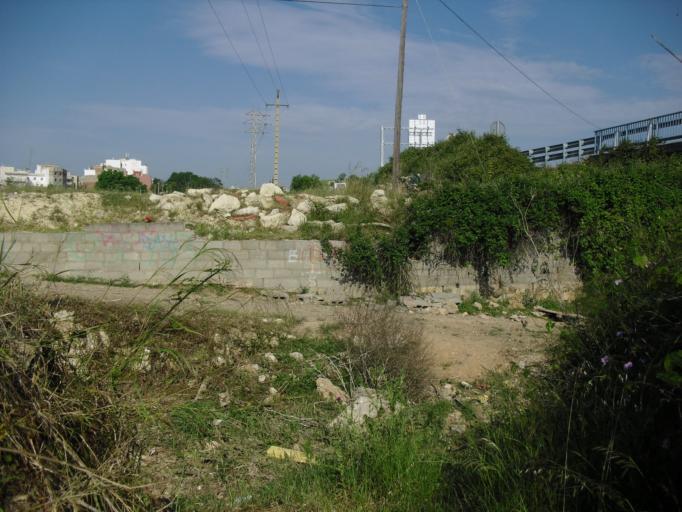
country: ES
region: Catalonia
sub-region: Provincia de Barcelona
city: Vilanova i la Geltru
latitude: 41.2366
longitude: 1.7315
